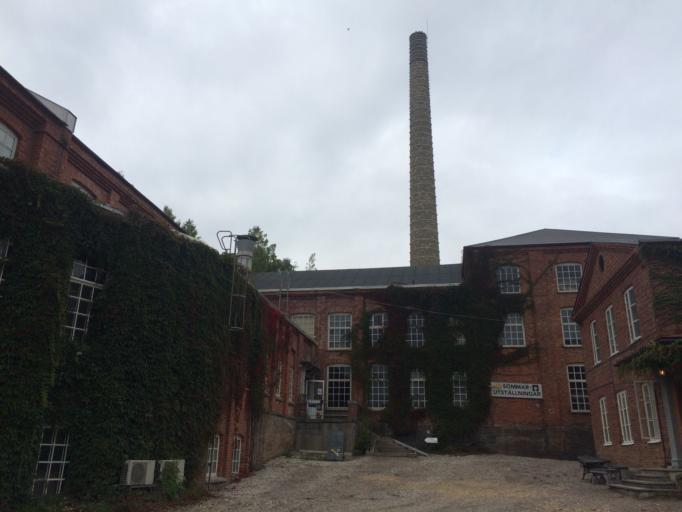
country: SE
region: Vaestra Goetaland
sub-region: Bengtsfors Kommun
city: Dals Langed
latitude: 58.9959
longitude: 12.4686
